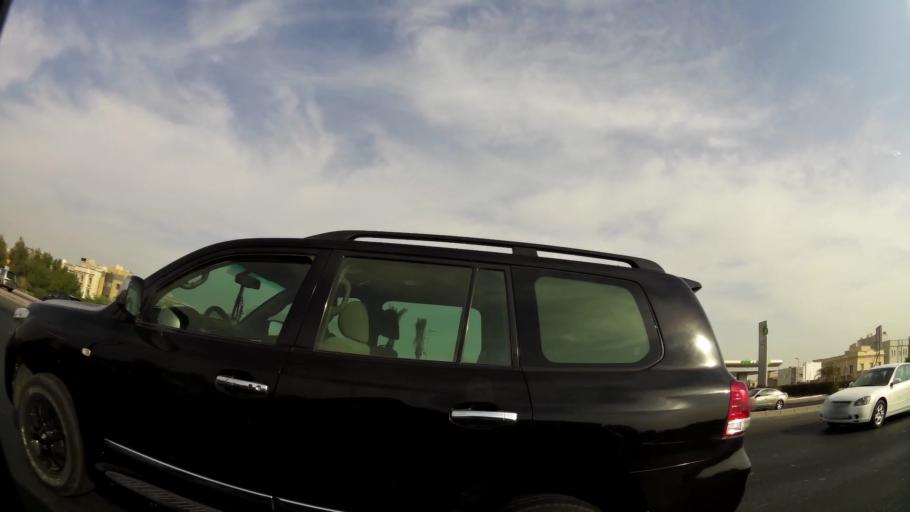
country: KW
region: Mubarak al Kabir
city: Sabah as Salim
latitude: 29.2651
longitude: 48.0279
